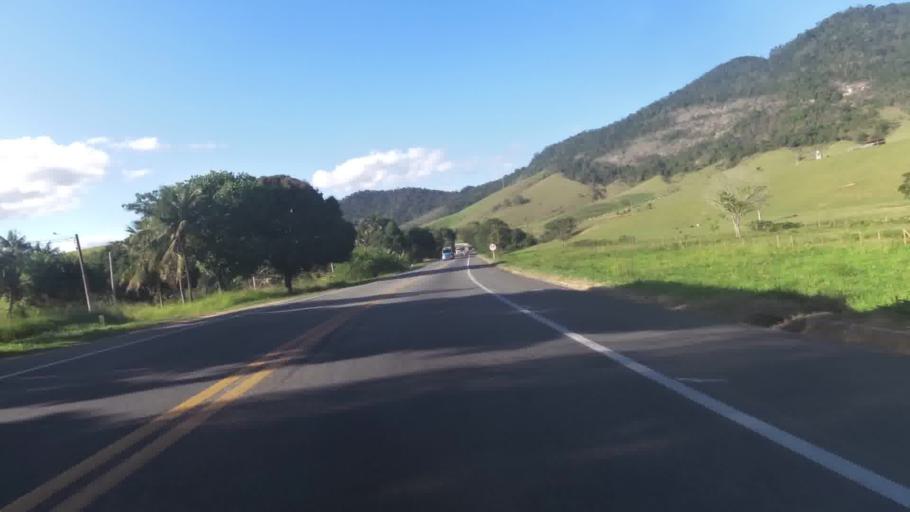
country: BR
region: Espirito Santo
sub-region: Iconha
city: Iconha
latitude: -20.7622
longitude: -40.7600
